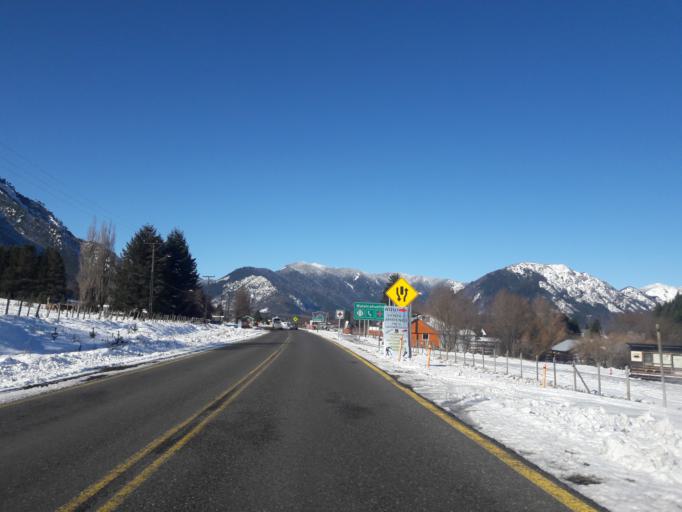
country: CL
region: Araucania
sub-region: Provincia de Cautin
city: Vilcun
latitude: -38.4708
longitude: -71.5796
